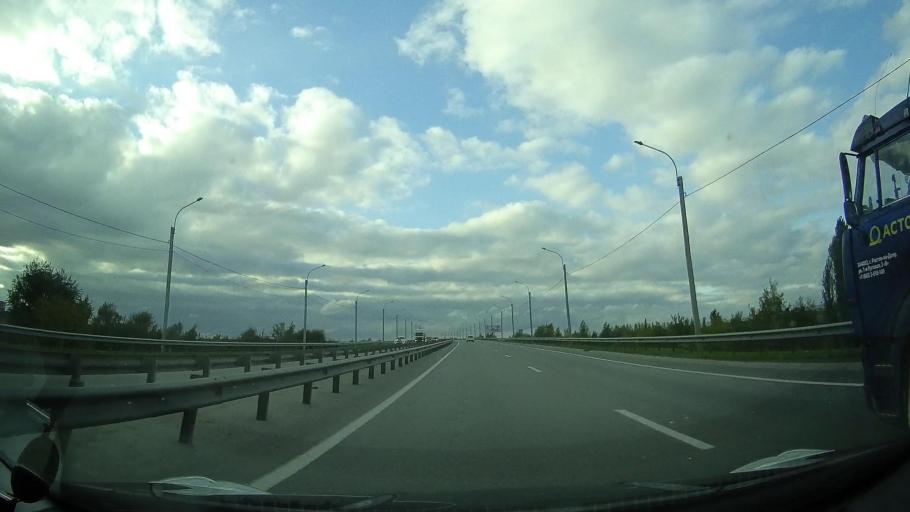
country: RU
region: Rostov
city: Bataysk
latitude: 47.1606
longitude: 39.7644
